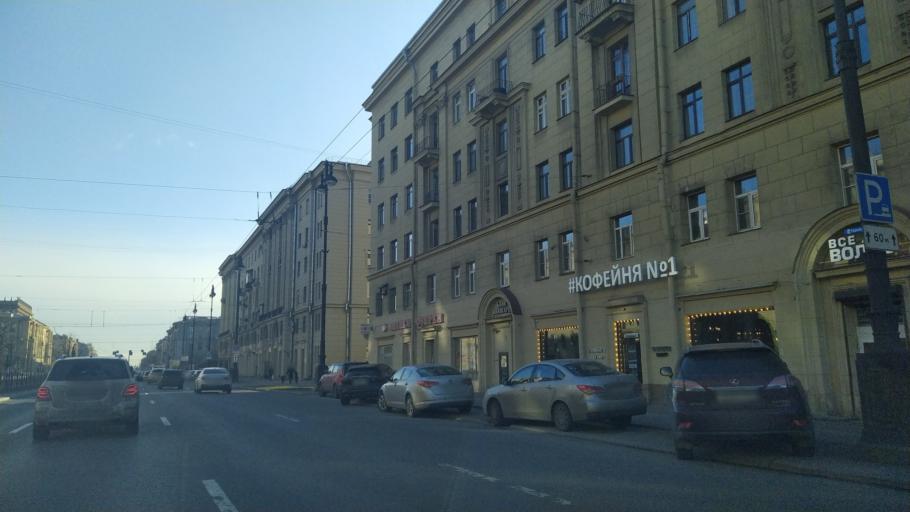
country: RU
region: St.-Petersburg
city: Kupchino
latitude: 59.8634
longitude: 30.3197
